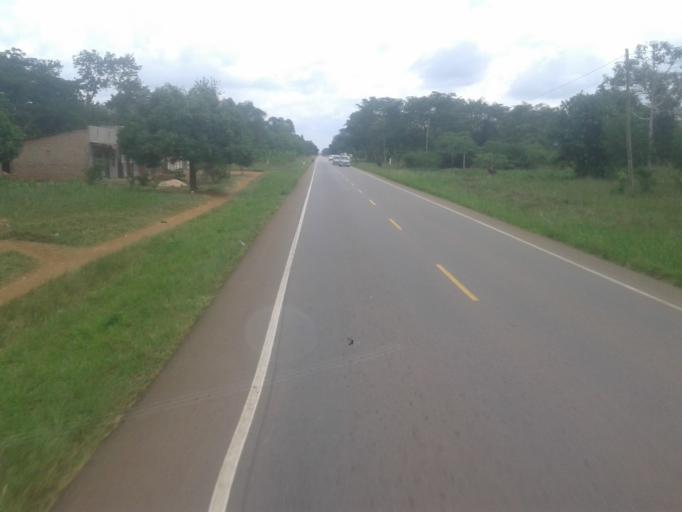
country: UG
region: Central Region
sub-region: Nakasongola District
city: Nakasongola
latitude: 1.0814
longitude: 32.4664
